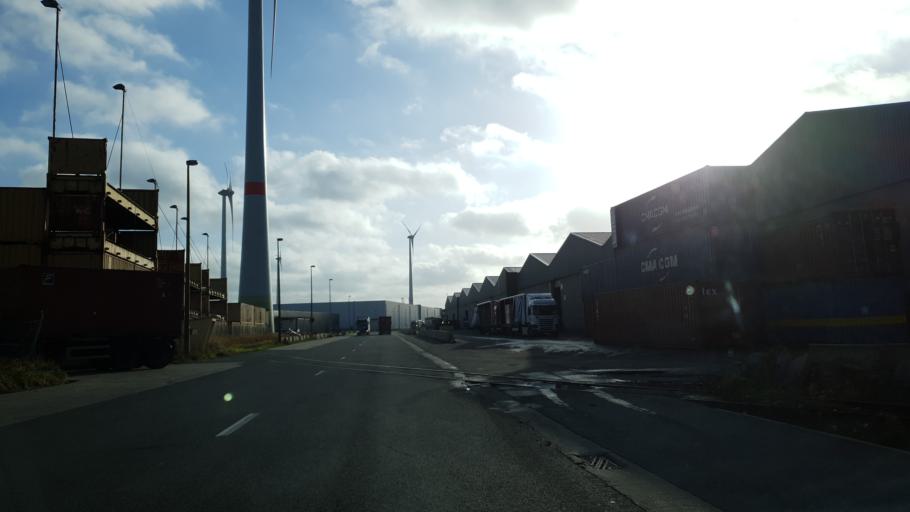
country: BE
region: Flanders
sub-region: Provincie Antwerpen
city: Stabroek
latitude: 51.2951
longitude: 4.3437
